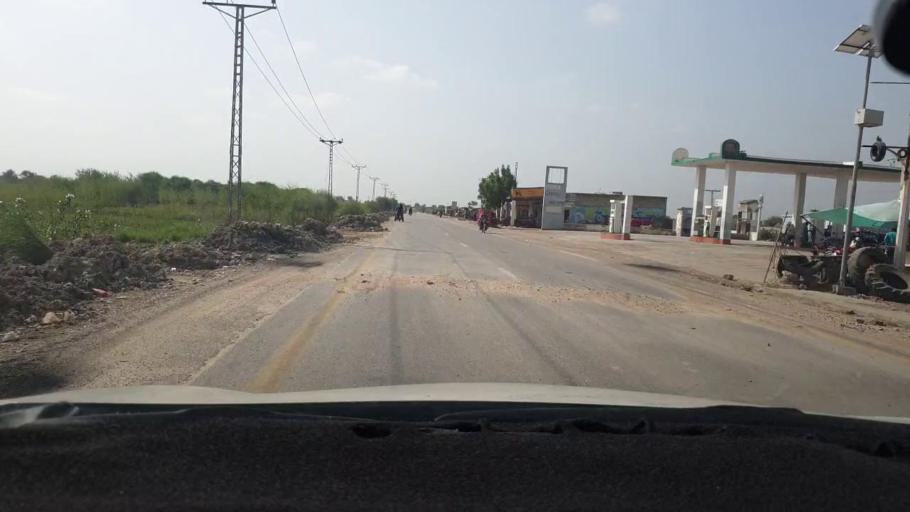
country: PK
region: Sindh
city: Mirpur Khas
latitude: 25.7716
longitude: 69.0713
